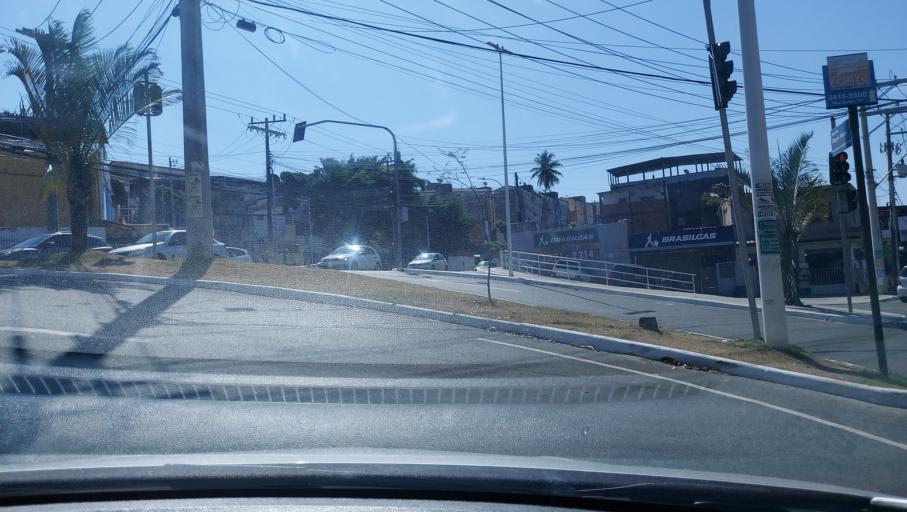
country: BR
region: Bahia
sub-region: Salvador
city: Salvador
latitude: -12.9606
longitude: -38.4393
